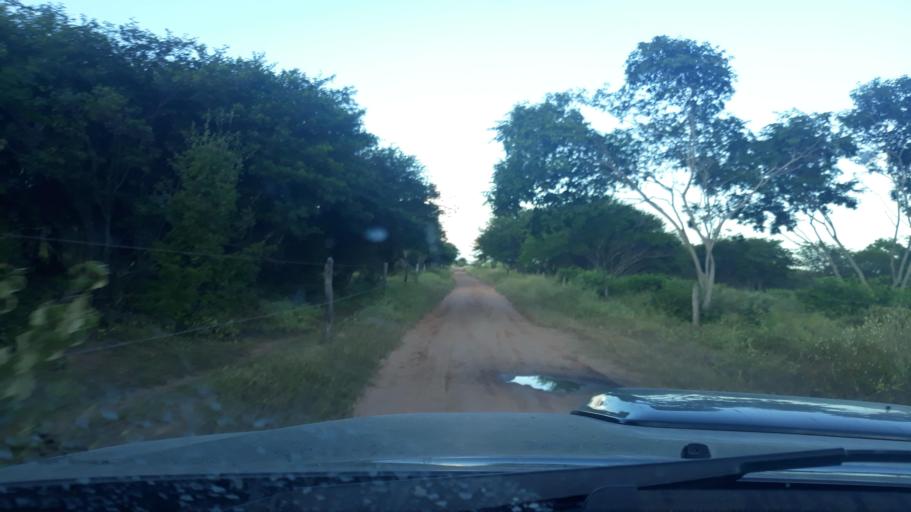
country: BR
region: Bahia
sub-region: Riacho De Santana
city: Riacho de Santana
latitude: -13.8594
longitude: -43.0671
